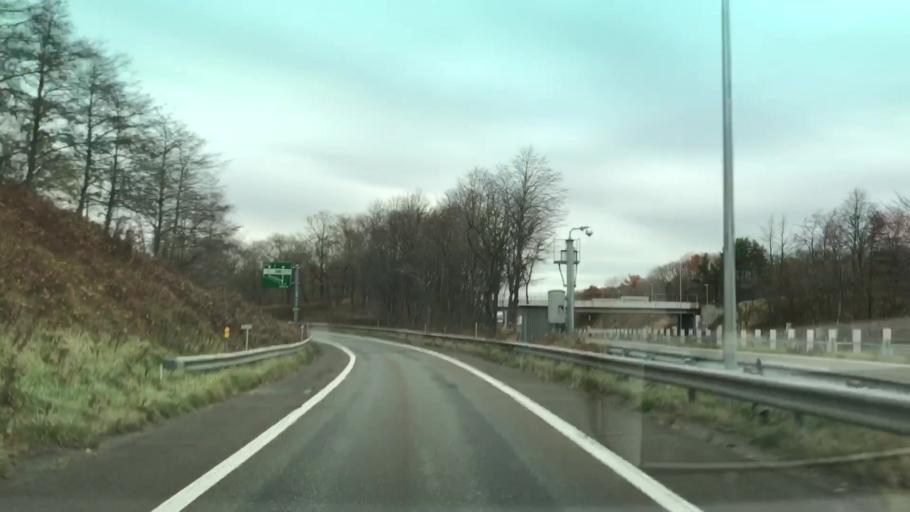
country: JP
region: Hokkaido
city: Tomakomai
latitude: 42.7113
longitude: 141.6524
